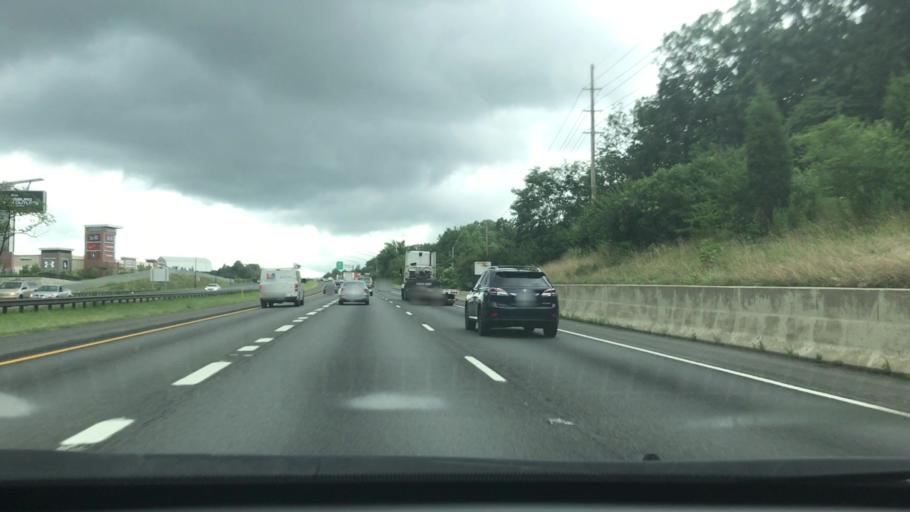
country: US
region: Maryland
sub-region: Montgomery County
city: Clarksburg
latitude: 39.2247
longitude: -77.2809
